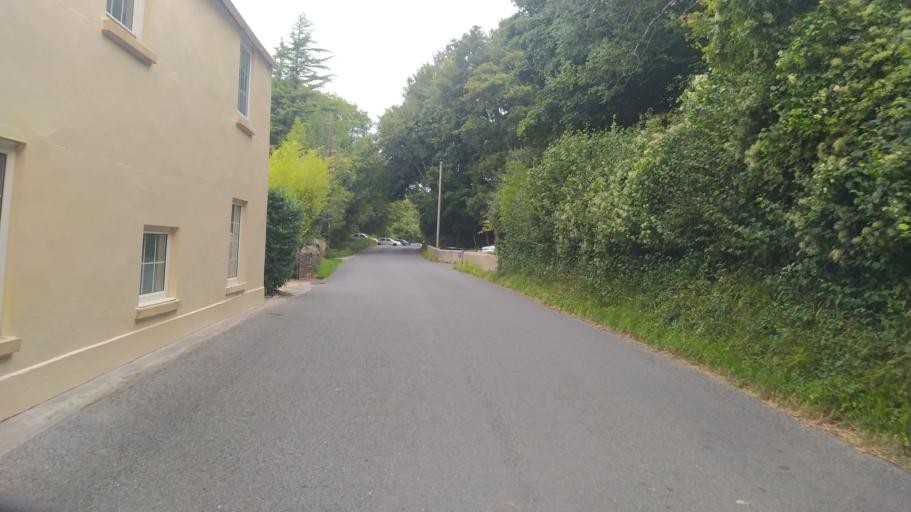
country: GB
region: England
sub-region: Dorset
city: Dorchester
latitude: 50.7751
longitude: -2.4058
